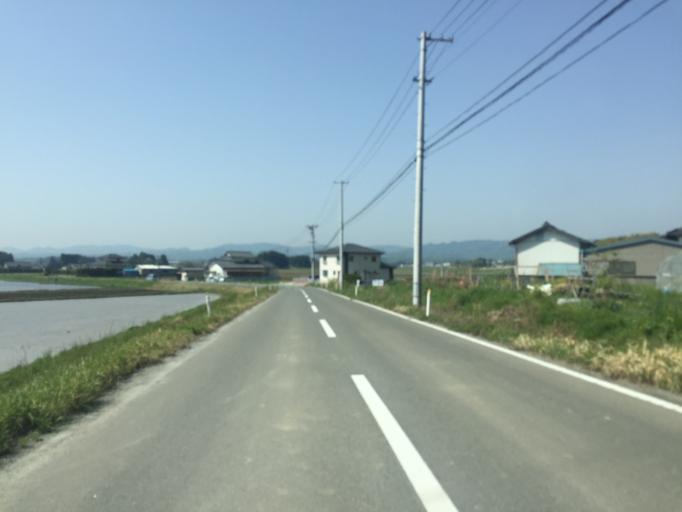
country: JP
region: Miyagi
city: Marumori
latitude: 37.7774
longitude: 140.9573
